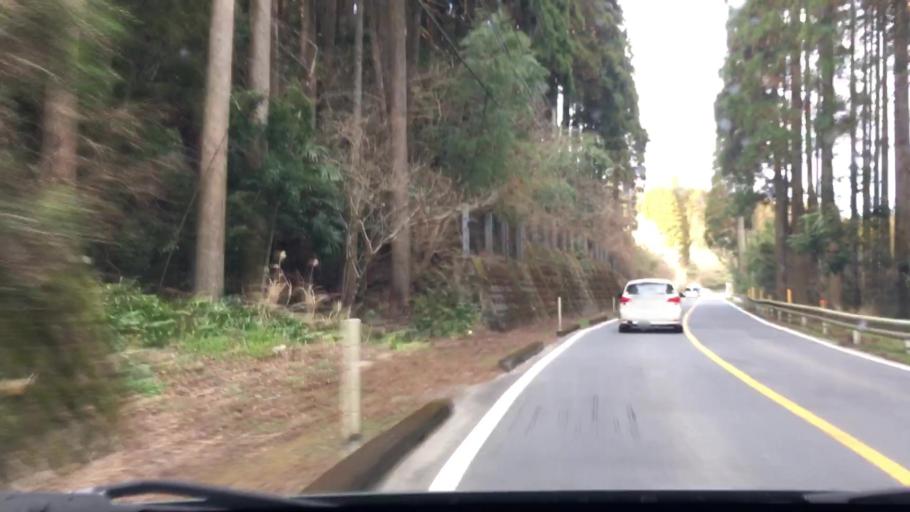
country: JP
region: Miyazaki
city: Nichinan
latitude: 31.7279
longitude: 131.3302
